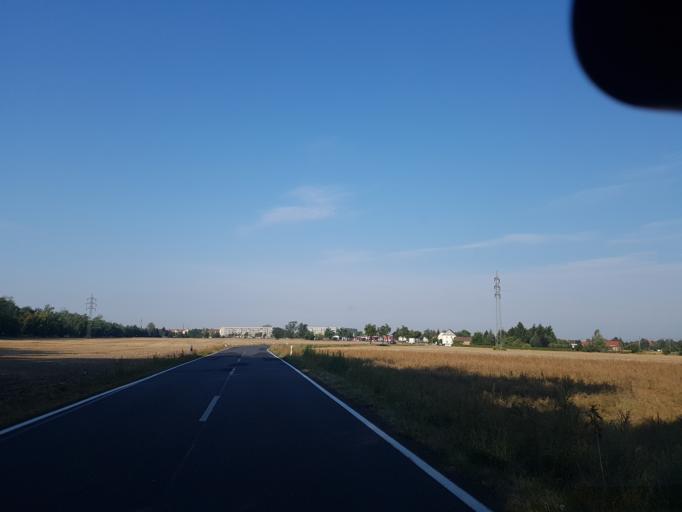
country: DE
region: Saxony
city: Nauwalde
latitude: 51.4211
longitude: 13.4668
